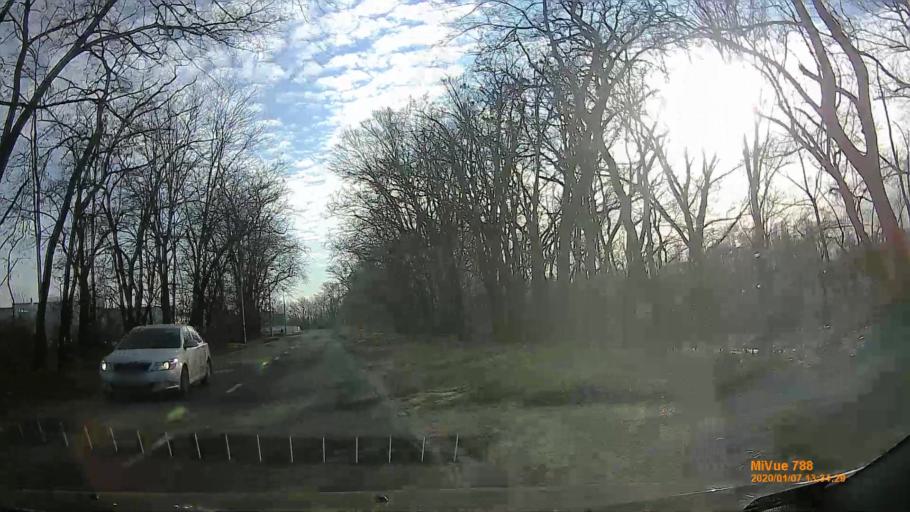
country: HU
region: Gyor-Moson-Sopron
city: Gyor
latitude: 47.6999
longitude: 17.6698
